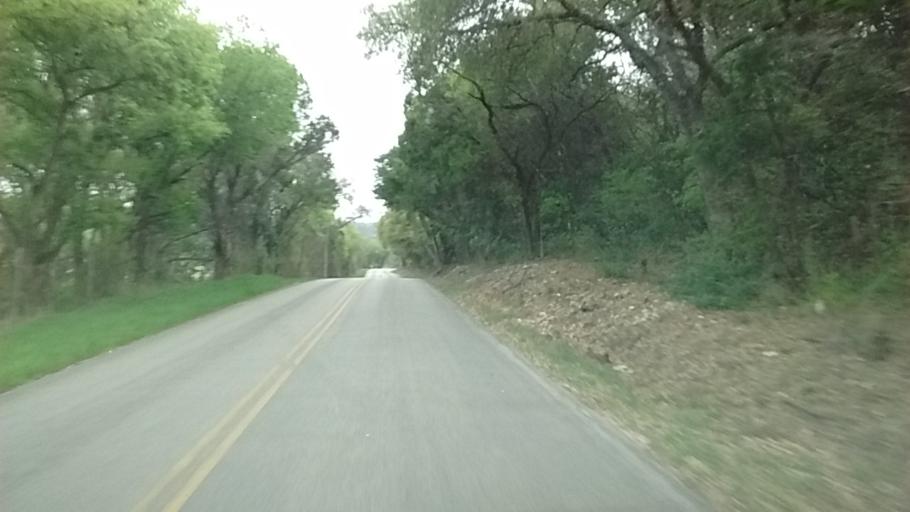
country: US
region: Texas
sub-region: Comal County
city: Canyon Lake
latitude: 29.8118
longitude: -98.1744
